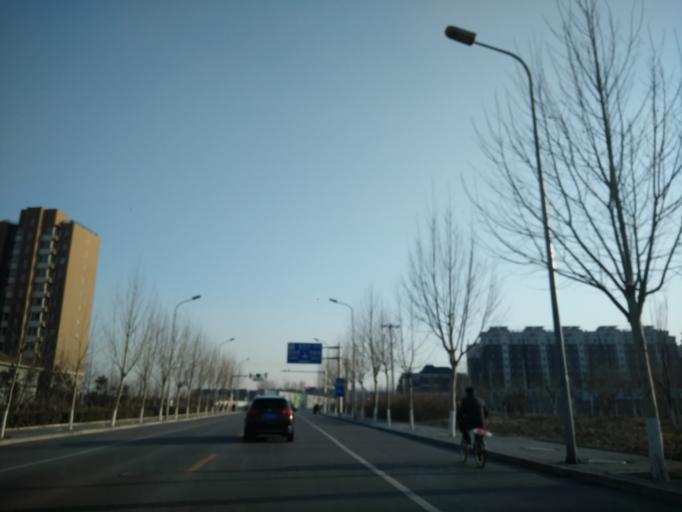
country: CN
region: Beijing
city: Yinghai
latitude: 39.7096
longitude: 116.3978
